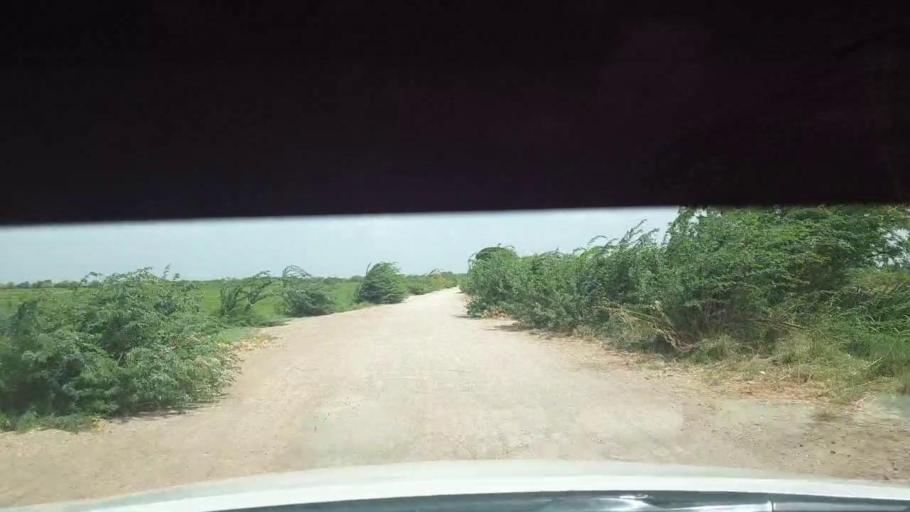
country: PK
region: Sindh
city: Kadhan
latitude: 24.4998
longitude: 68.9812
